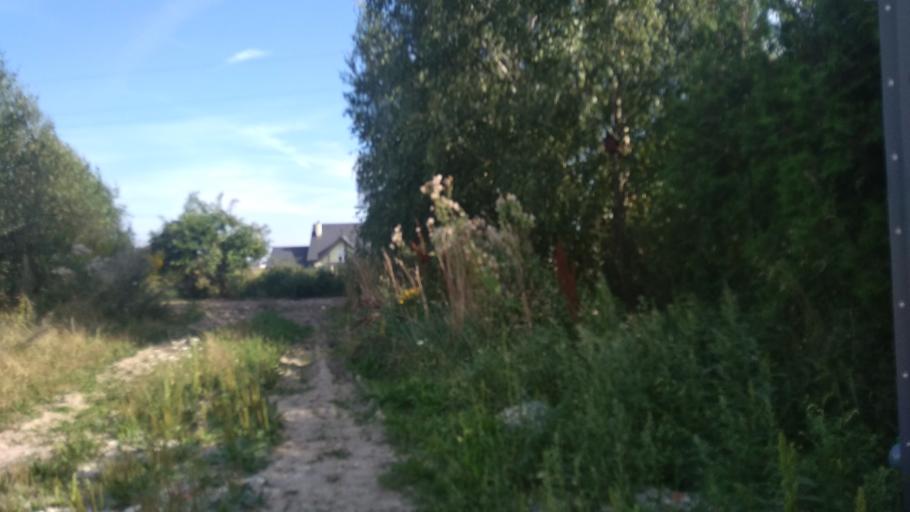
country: PL
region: Kujawsko-Pomorskie
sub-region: Powiat bydgoski
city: Osielsko
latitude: 53.2189
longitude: 18.1474
